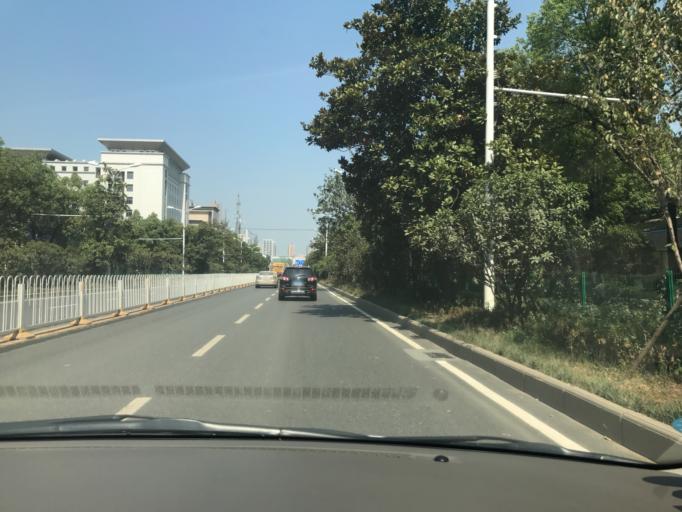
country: CN
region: Hubei
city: Shilipu
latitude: 30.5608
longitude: 114.2183
